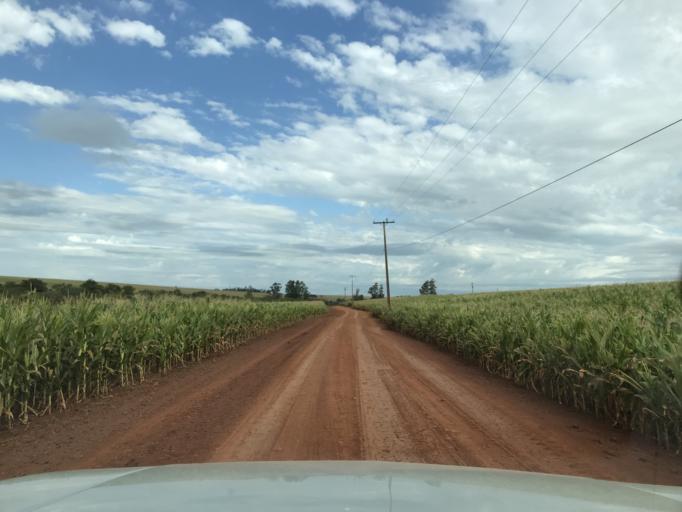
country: BR
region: Parana
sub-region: Palotina
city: Palotina
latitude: -24.3166
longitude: -53.8069
